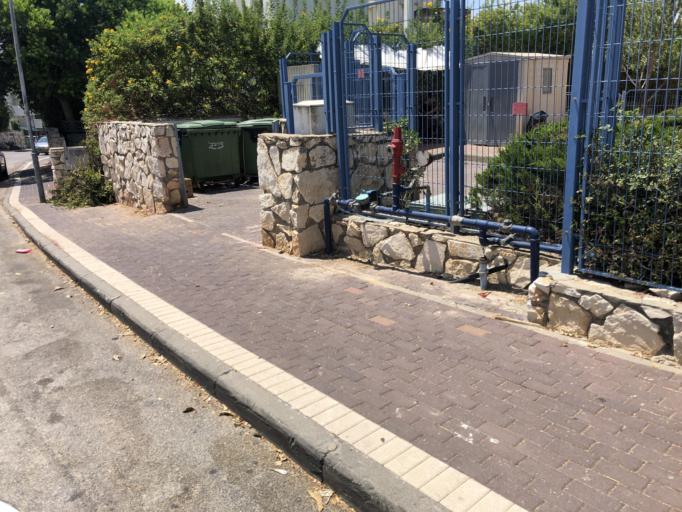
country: IL
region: Haifa
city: Daliyat el Karmil
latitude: 32.6377
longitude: 35.0889
